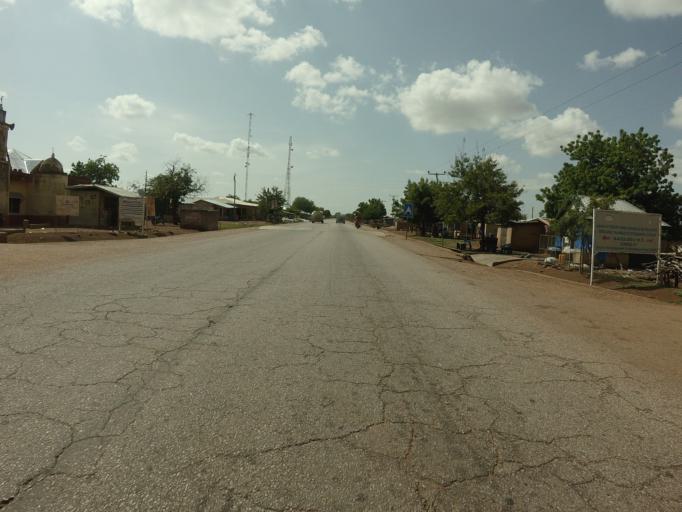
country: GH
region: Northern
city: Savelugu
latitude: 9.8697
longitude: -0.8715
